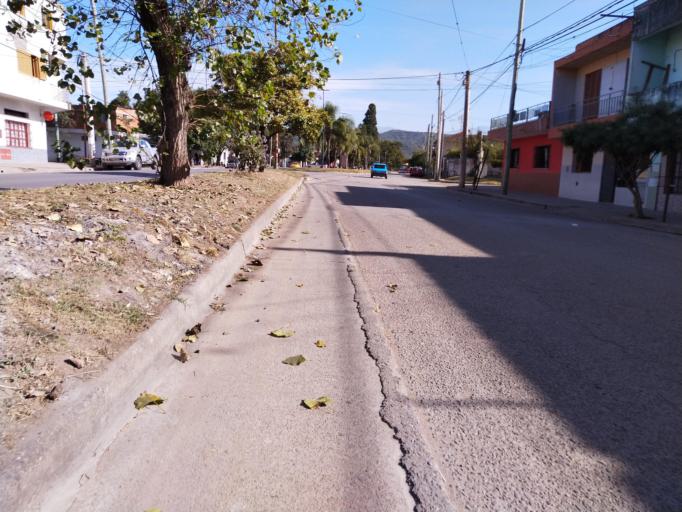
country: AR
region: Jujuy
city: San Salvador de Jujuy
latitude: -24.1998
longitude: -65.2814
